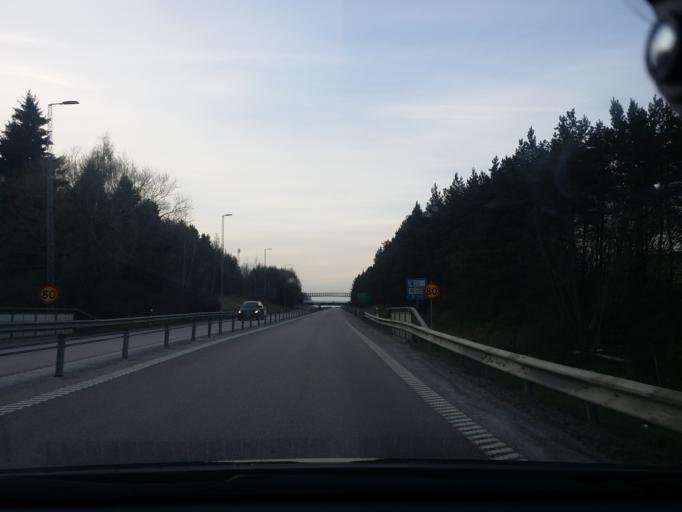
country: SE
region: Uppsala
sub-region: Enkopings Kommun
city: Enkoping
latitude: 59.6399
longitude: 17.0550
